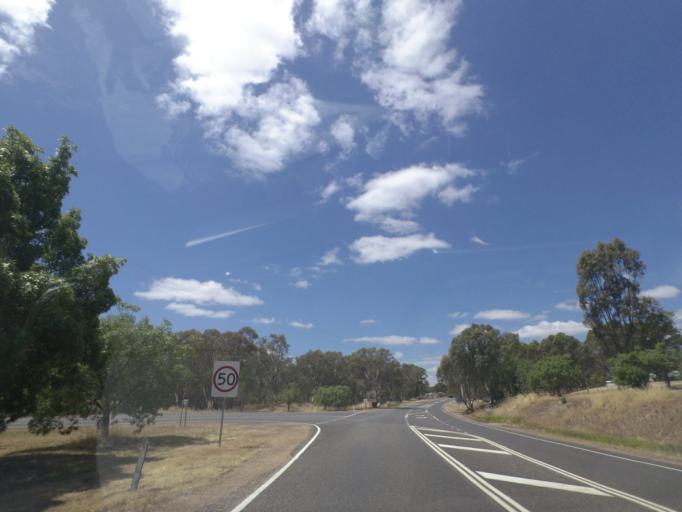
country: AU
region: Victoria
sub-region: Wangaratta
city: Wangaratta
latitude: -36.4645
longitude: 146.2161
